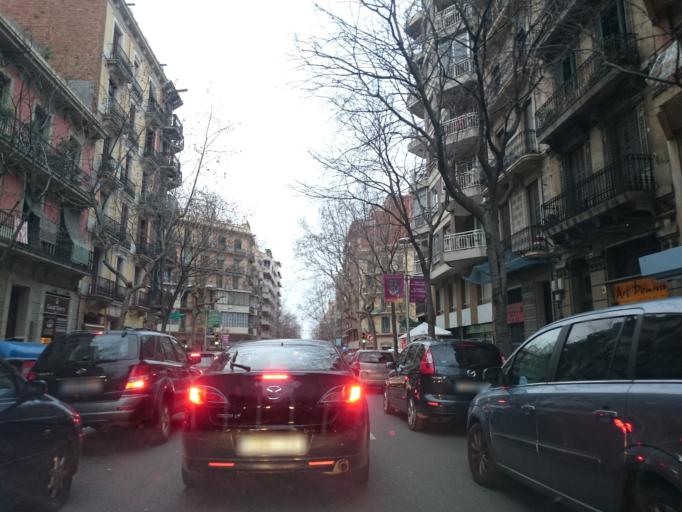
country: ES
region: Catalonia
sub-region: Provincia de Barcelona
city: Horta-Guinardo
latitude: 41.4022
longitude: 2.1749
